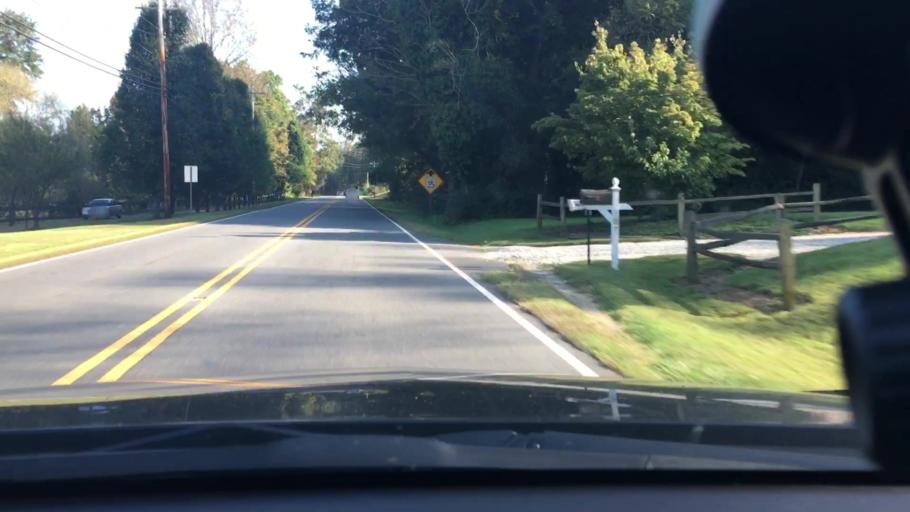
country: US
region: North Carolina
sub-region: Rutherford County
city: Rutherfordton
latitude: 35.3858
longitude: -81.9691
